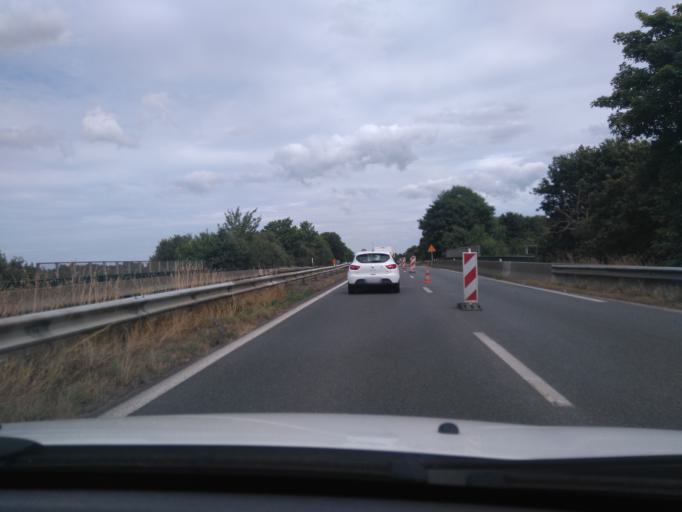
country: FR
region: Brittany
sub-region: Departement des Cotes-d'Armor
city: Plelo
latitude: 48.5302
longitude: -2.9636
